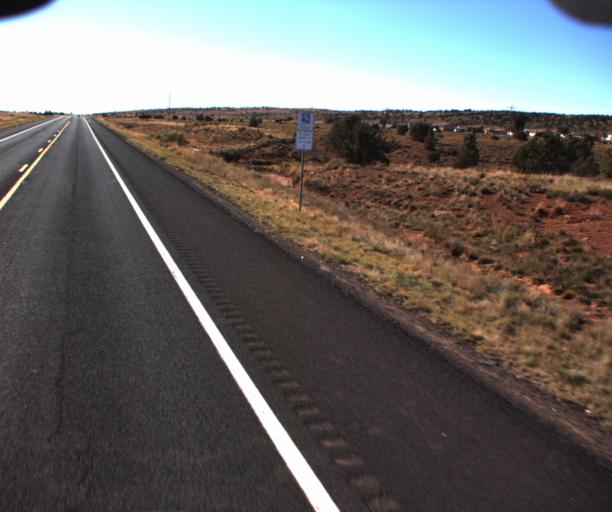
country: US
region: Arizona
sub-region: Coconino County
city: Tuba City
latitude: 36.3891
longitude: -111.5232
